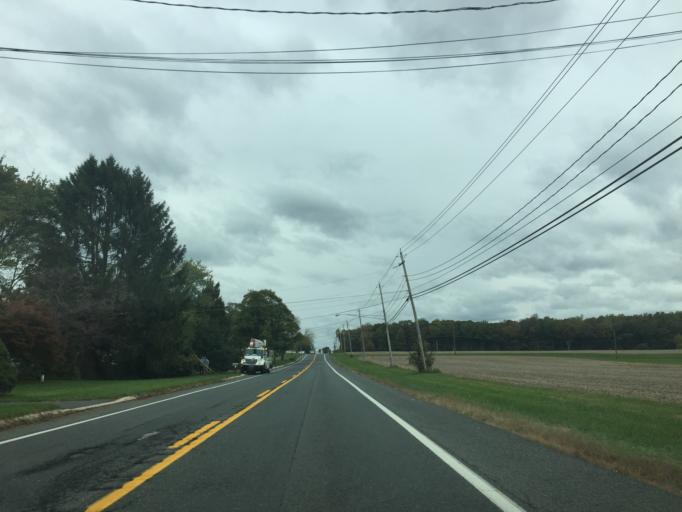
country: US
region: Maryland
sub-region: Harford County
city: Riverside
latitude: 39.5018
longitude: -76.2659
